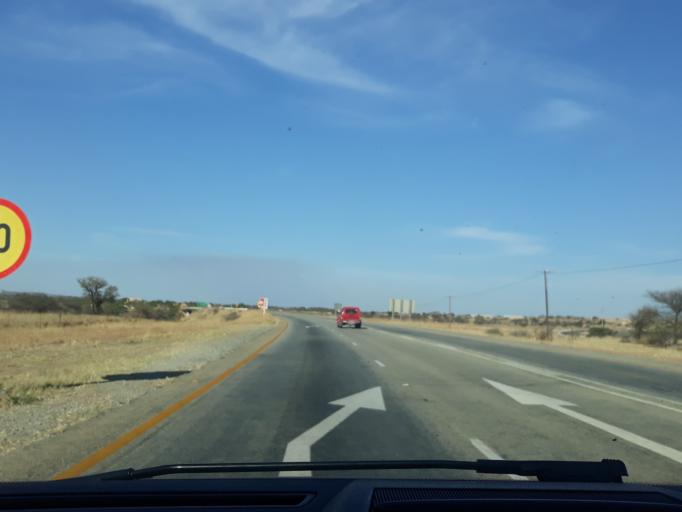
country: ZA
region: Limpopo
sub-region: Capricorn District Municipality
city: Polokwane
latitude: -23.9470
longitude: 29.4109
